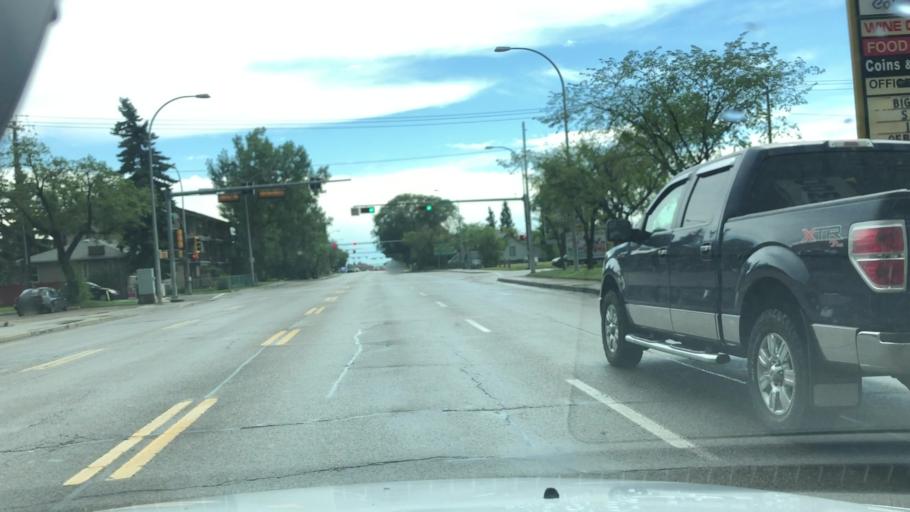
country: CA
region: Alberta
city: Edmonton
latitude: 53.5881
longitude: -113.5412
